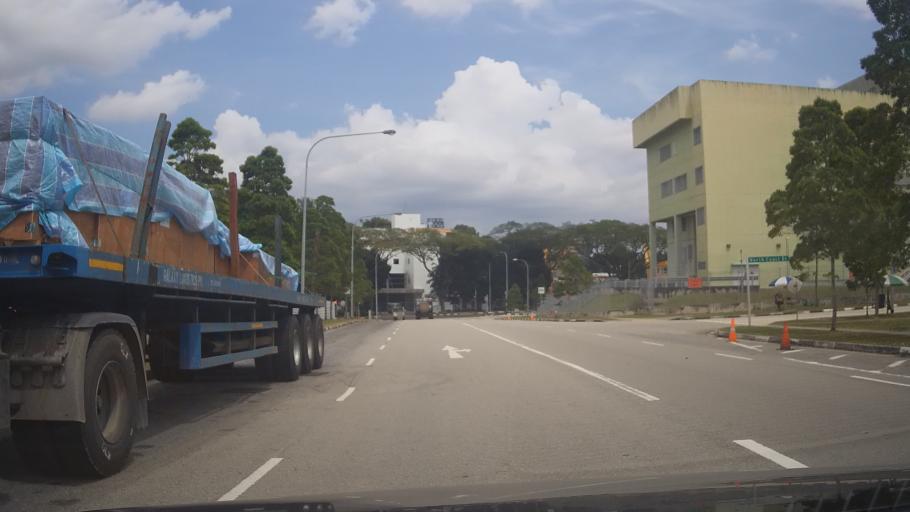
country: MY
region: Johor
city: Johor Bahru
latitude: 1.4570
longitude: 103.7939
